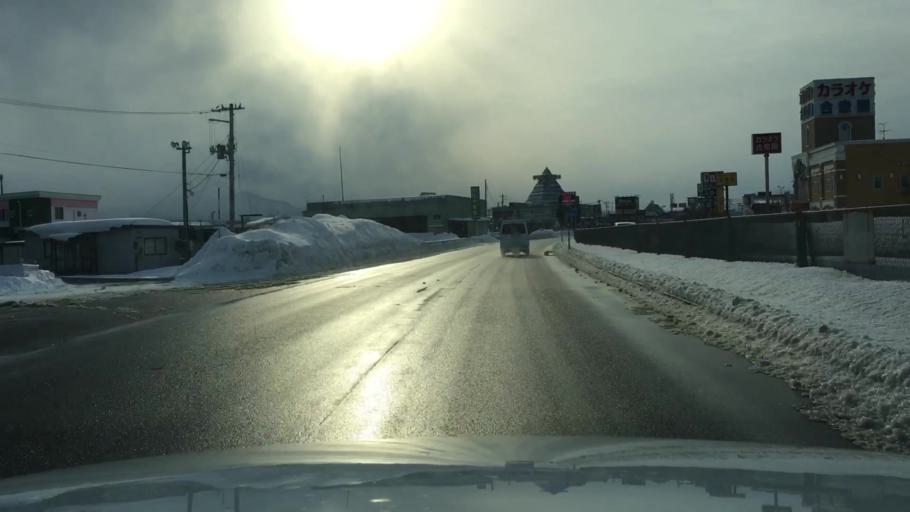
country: JP
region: Aomori
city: Hirosaki
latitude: 40.5979
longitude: 140.5121
